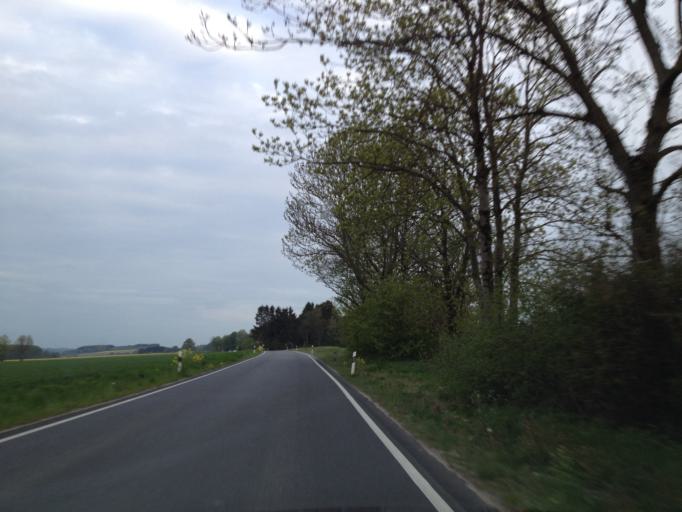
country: DE
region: North Rhine-Westphalia
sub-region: Regierungsbezirk Arnsberg
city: Anrochte
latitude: 51.5104
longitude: 8.2471
